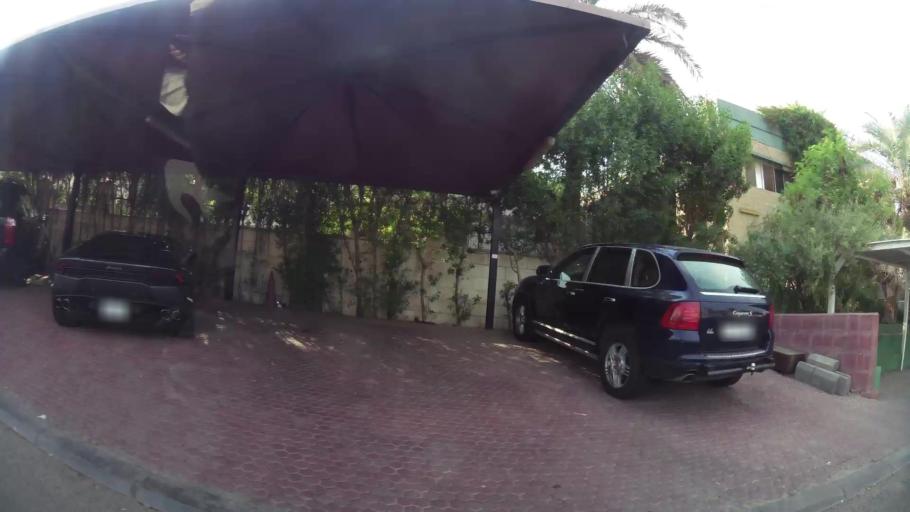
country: KW
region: Al Asimah
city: Ash Shamiyah
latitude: 29.3137
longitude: 47.9837
